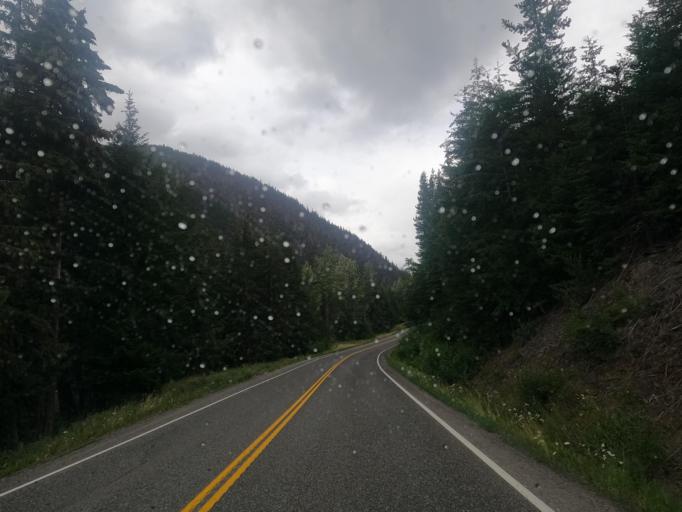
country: CA
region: British Columbia
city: Lillooet
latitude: 50.4890
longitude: -122.2026
